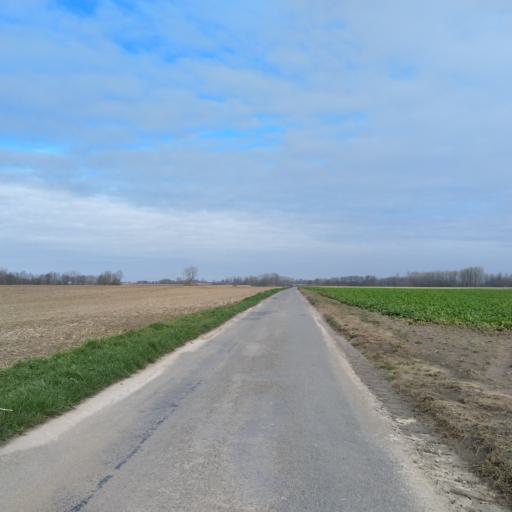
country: BE
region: Wallonia
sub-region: Province du Hainaut
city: Lens
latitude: 50.5702
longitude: 3.9010
